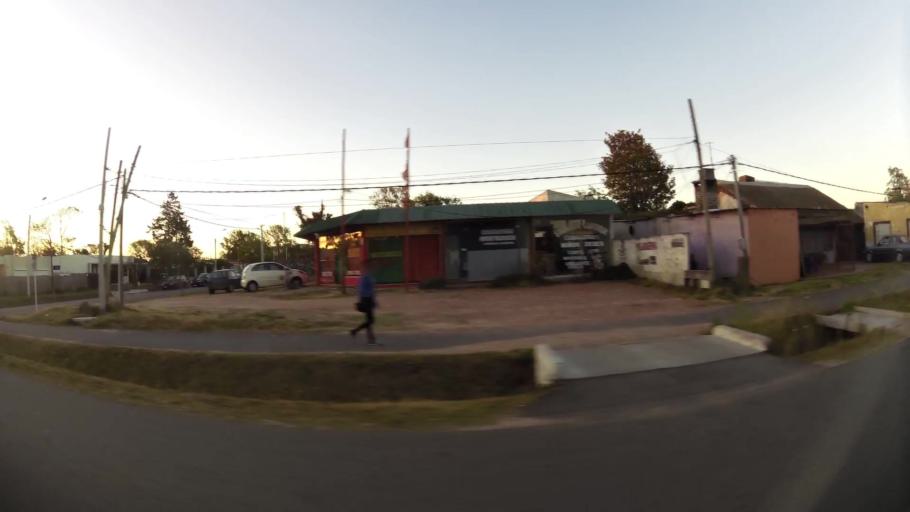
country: UY
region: Canelones
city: Barra de Carrasco
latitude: -34.8355
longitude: -55.9632
